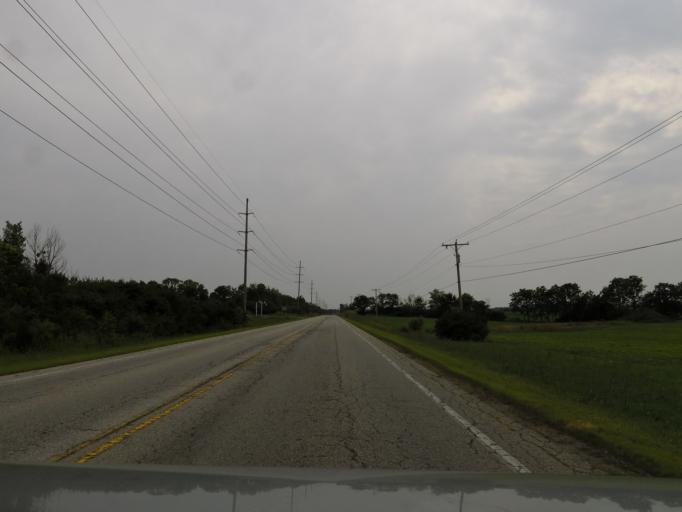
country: US
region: Ohio
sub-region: Clinton County
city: Wilmington
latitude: 39.4107
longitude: -83.8470
